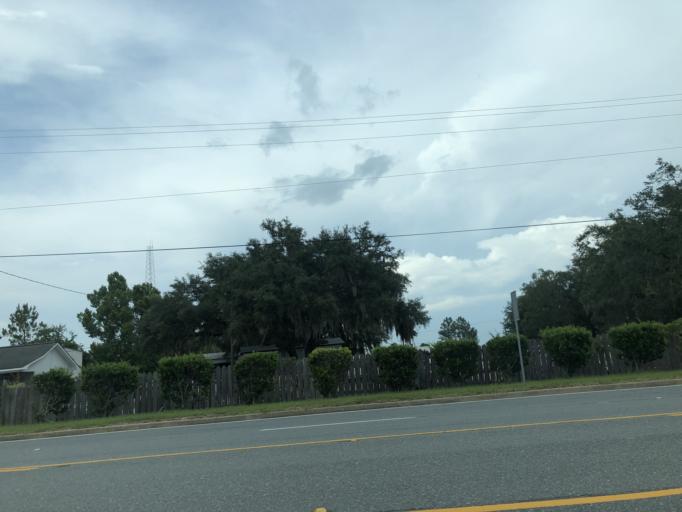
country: US
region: Georgia
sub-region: Wayne County
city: Jesup
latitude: 31.6188
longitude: -81.8978
